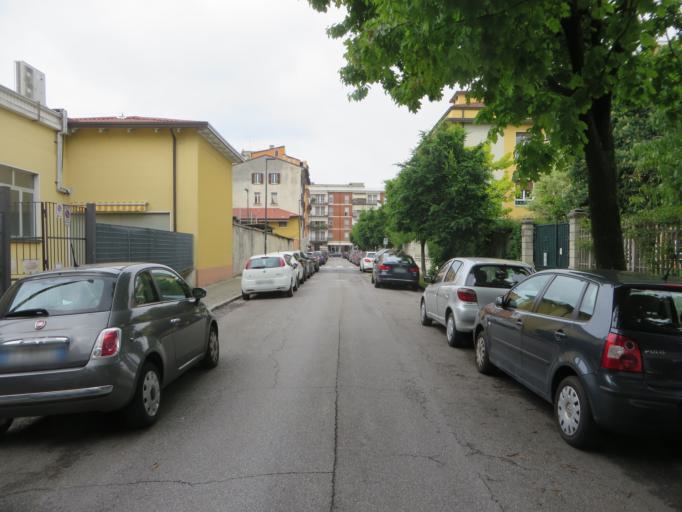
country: IT
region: Lombardy
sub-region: Provincia di Brescia
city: Brescia
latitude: 45.5265
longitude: 10.2252
